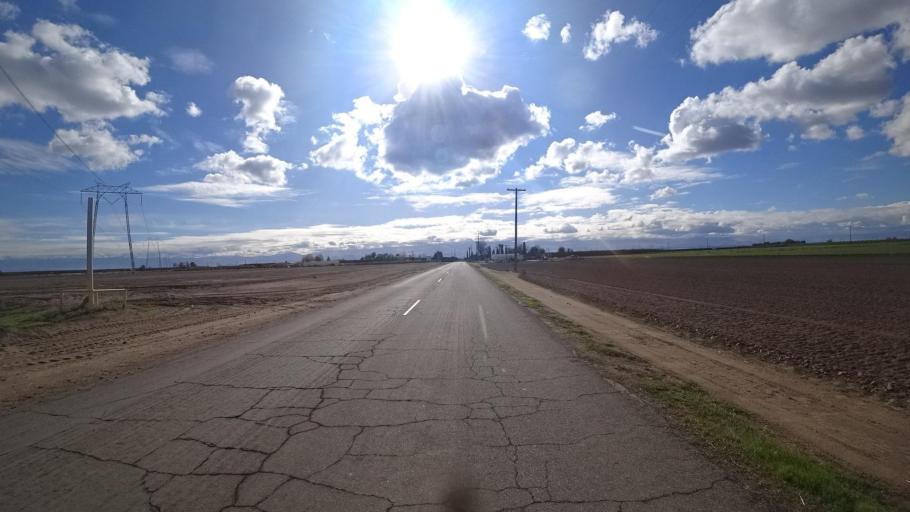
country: US
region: California
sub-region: Kern County
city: Greenfield
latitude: 35.2209
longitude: -119.0923
